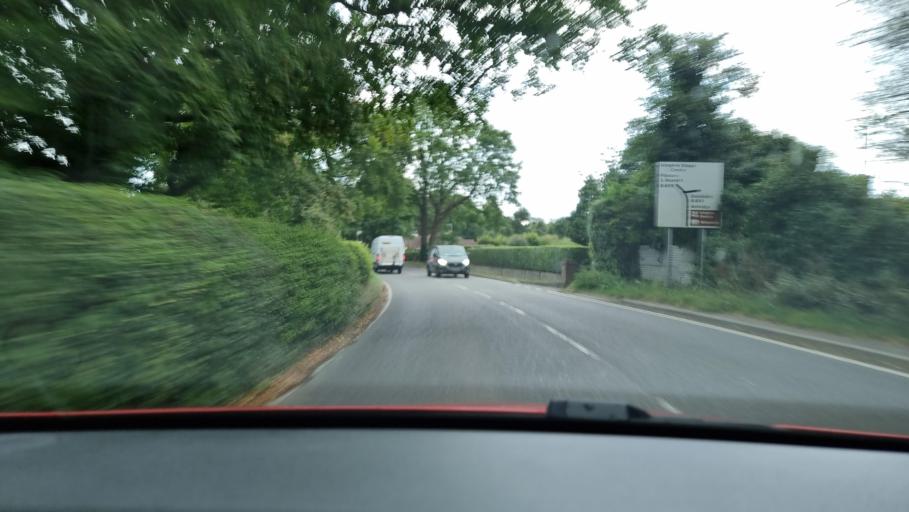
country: GB
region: England
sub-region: Buckinghamshire
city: Ivinghoe
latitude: 51.8333
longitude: -0.6263
